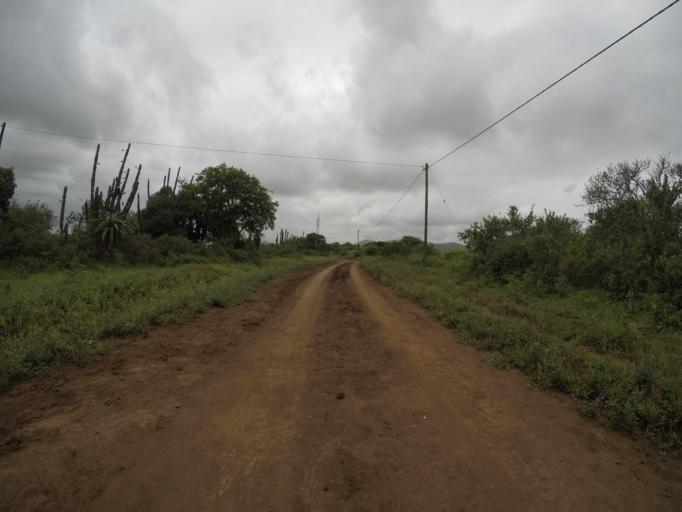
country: ZA
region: KwaZulu-Natal
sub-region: uThungulu District Municipality
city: Empangeni
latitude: -28.6018
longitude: 31.8461
